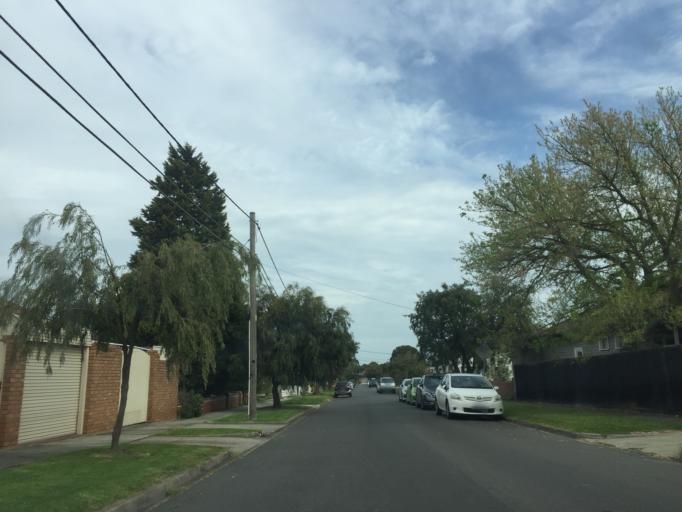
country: AU
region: Victoria
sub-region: Darebin
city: Preston
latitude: -37.7419
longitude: 145.0145
